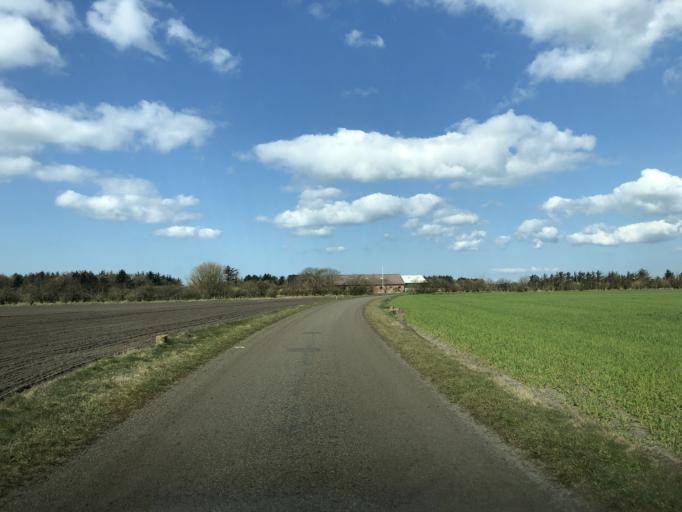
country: DK
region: Central Jutland
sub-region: Holstebro Kommune
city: Ulfborg
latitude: 56.3948
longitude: 8.1823
